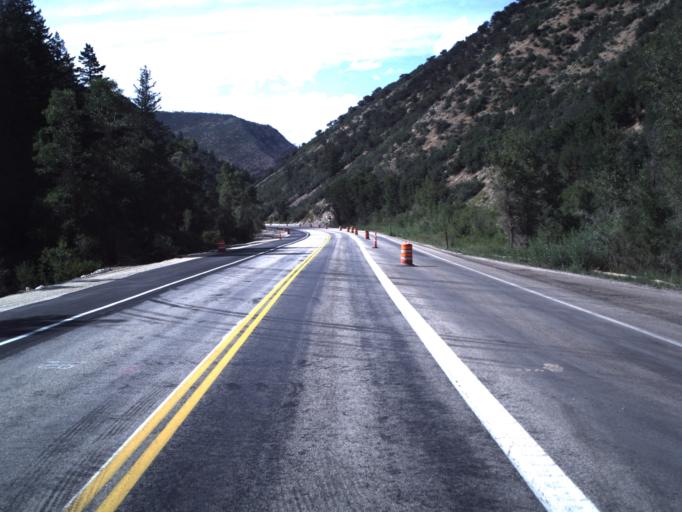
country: US
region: Utah
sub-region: Wasatch County
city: Heber
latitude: 40.3653
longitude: -111.2887
